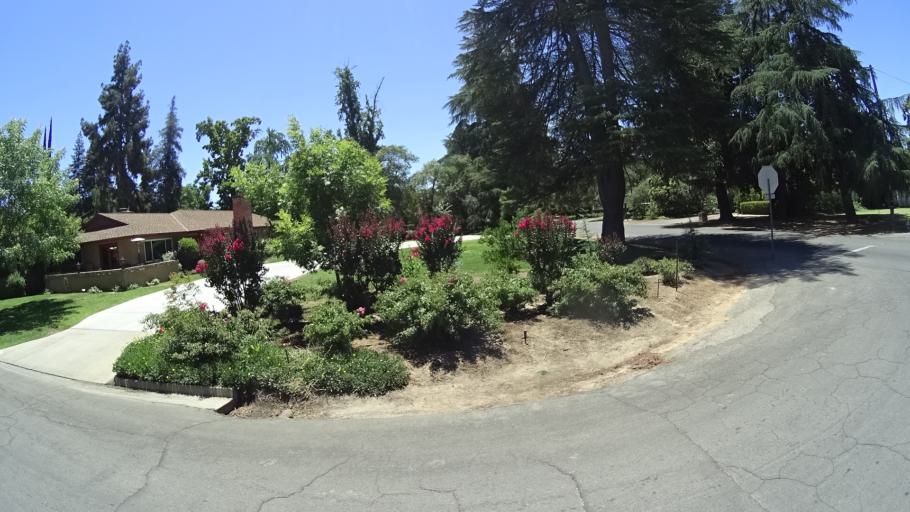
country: US
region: California
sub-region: Fresno County
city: Fresno
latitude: 36.7849
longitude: -119.8039
